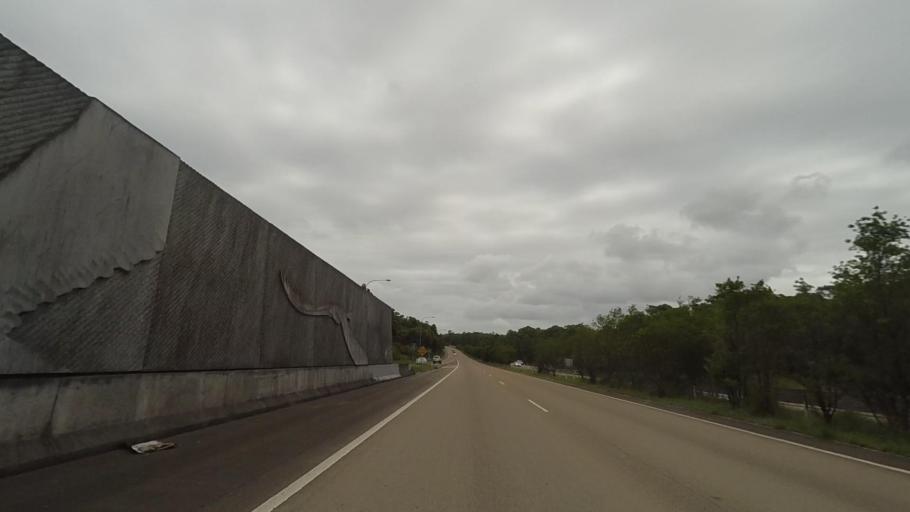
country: AU
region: New South Wales
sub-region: Lake Macquarie Shire
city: Kotara
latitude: -32.9600
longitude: 151.6780
